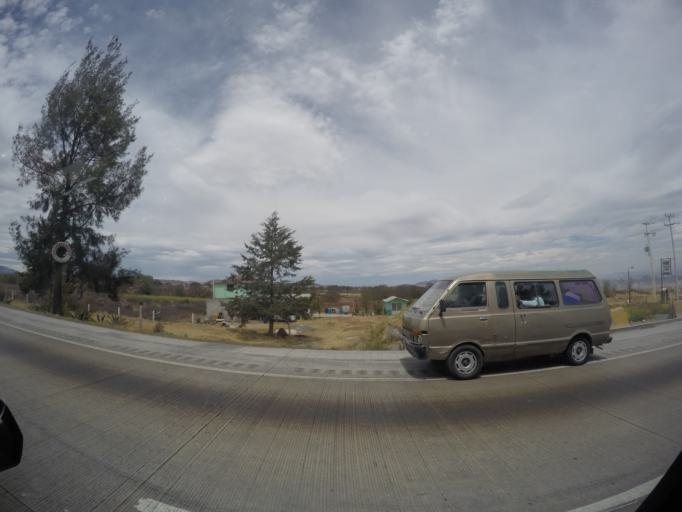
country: MX
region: Mexico
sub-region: Jilotepec
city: La Comunidad
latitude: 20.0376
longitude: -99.5649
